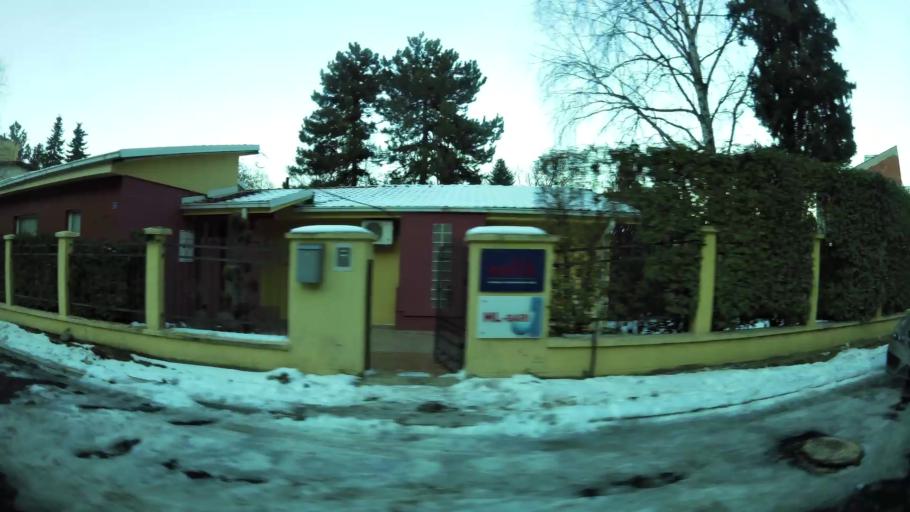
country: MK
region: Karpos
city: Skopje
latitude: 41.9903
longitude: 21.4104
